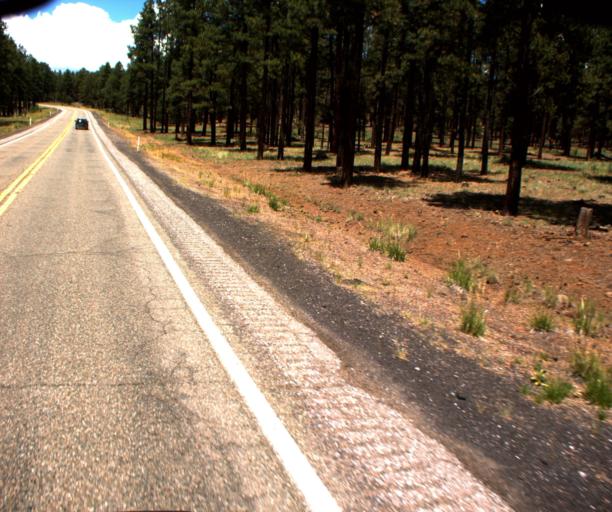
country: US
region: Arizona
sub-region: Coconino County
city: Flagstaff
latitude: 35.2817
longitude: -111.7495
